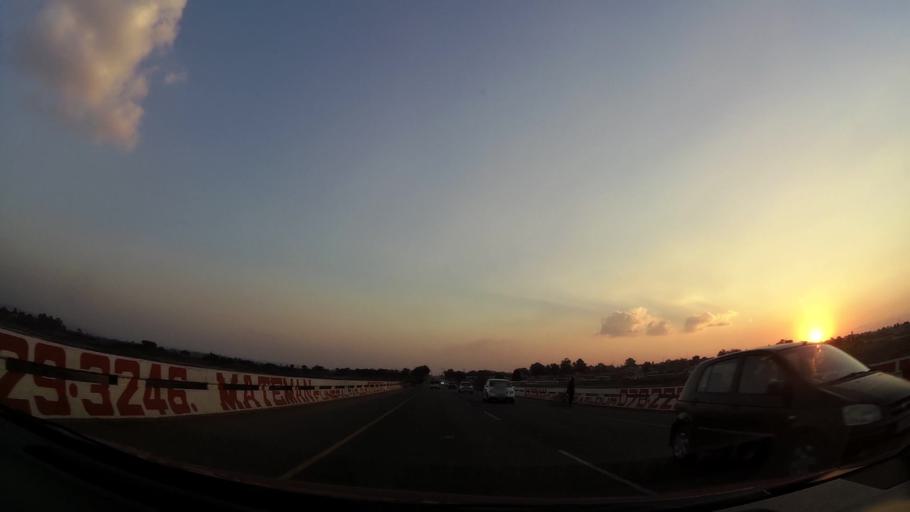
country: ZA
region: Gauteng
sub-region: City of Johannesburg Metropolitan Municipality
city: Soweto
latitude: -26.2900
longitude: 27.8856
